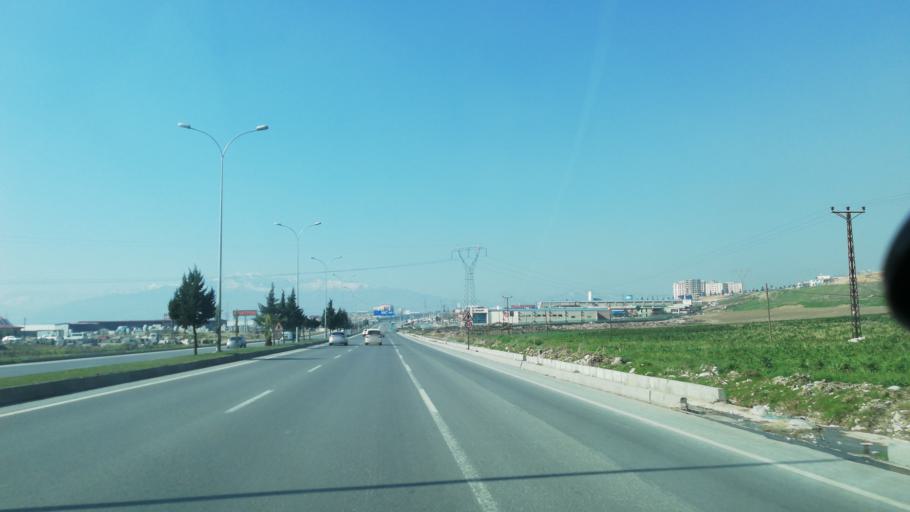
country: TR
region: Kahramanmaras
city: Kahramanmaras
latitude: 37.5648
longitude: 36.8983
